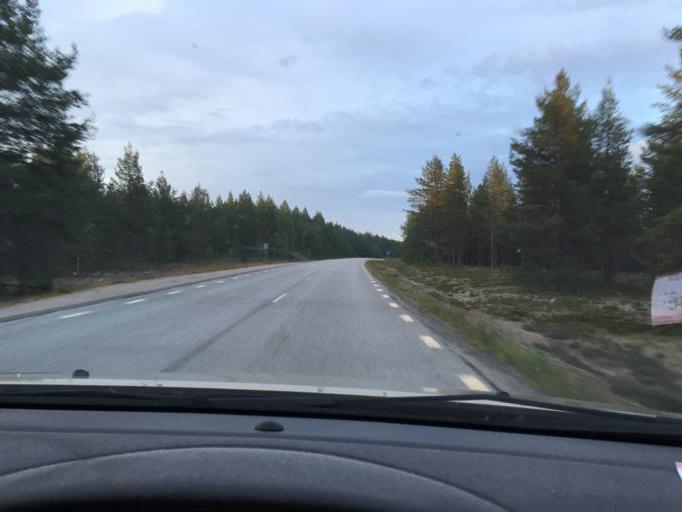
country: SE
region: Norrbotten
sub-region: Lulea Kommun
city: Ranea
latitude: 66.0489
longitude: 22.2513
